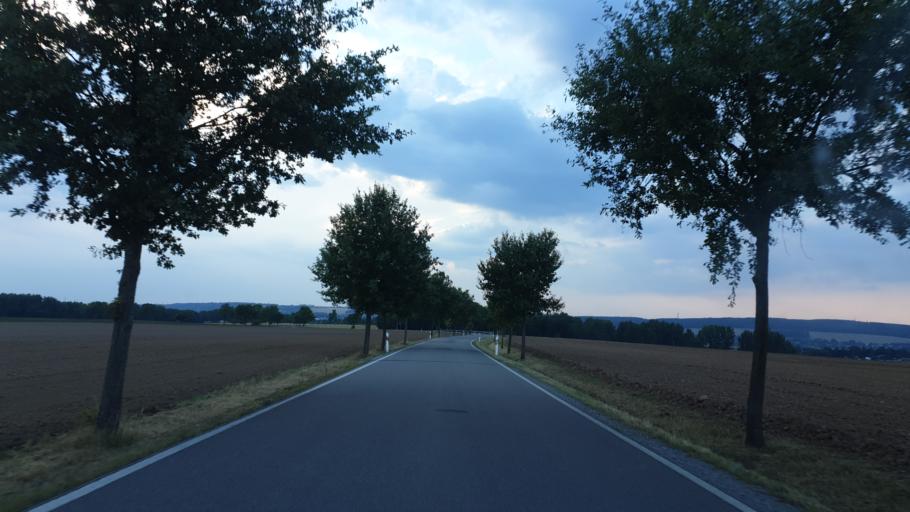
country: DE
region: Saxony
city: Niederdorf
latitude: 50.7850
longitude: 12.8031
